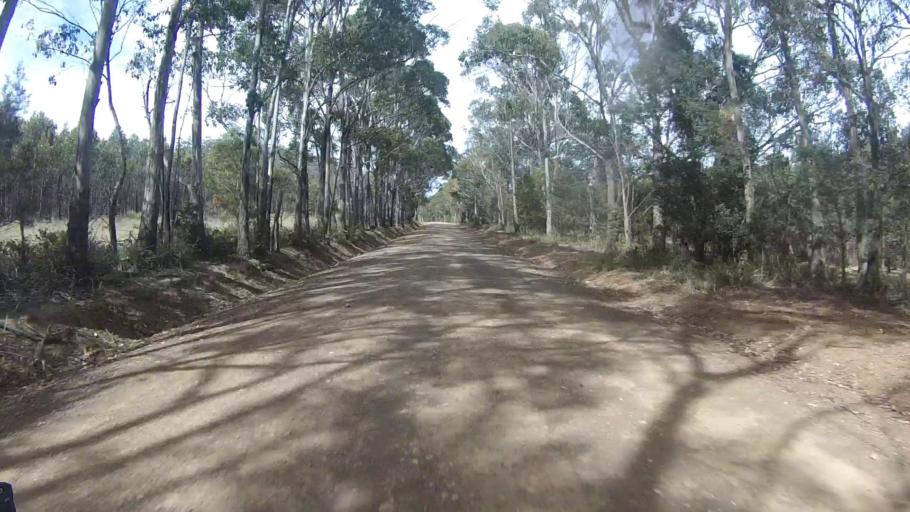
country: AU
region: Tasmania
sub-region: Sorell
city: Sorell
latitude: -42.6636
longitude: 147.8908
